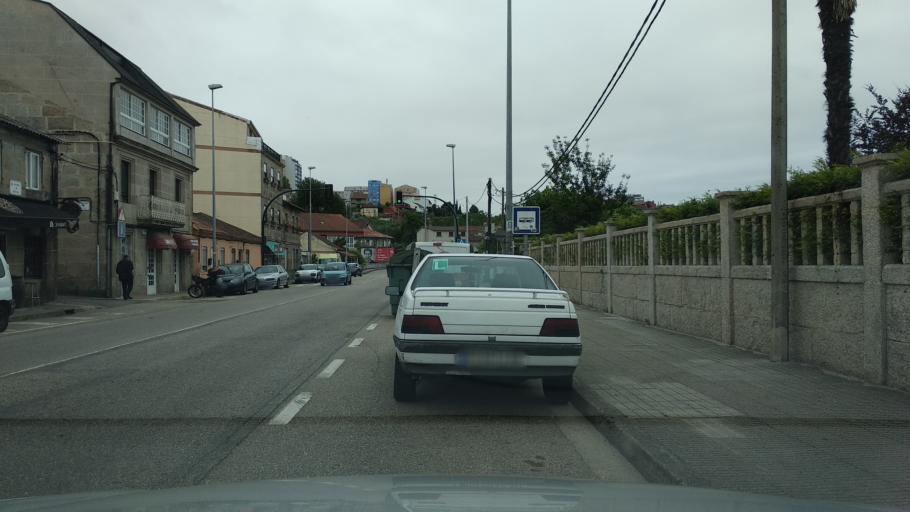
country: ES
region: Galicia
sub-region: Provincia de Pontevedra
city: Vigo
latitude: 42.2516
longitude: -8.6891
